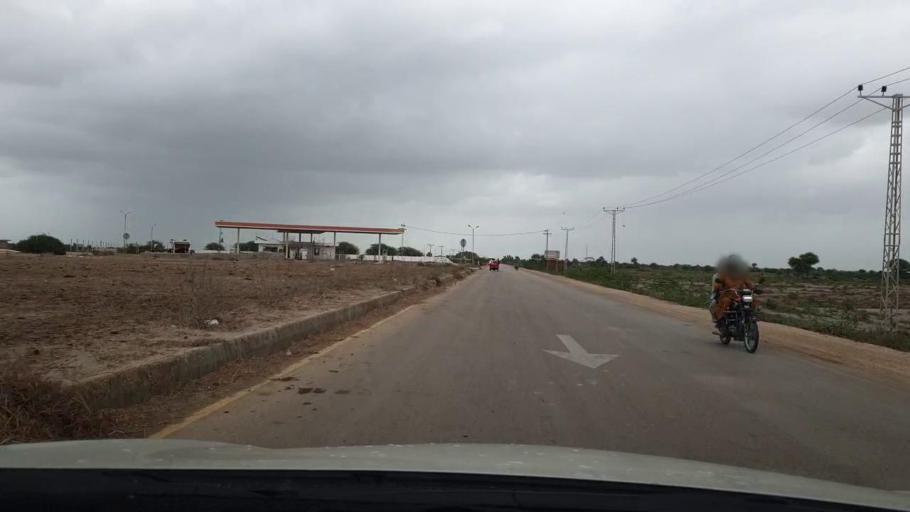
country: PK
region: Sindh
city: Badin
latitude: 24.6519
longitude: 68.7755
